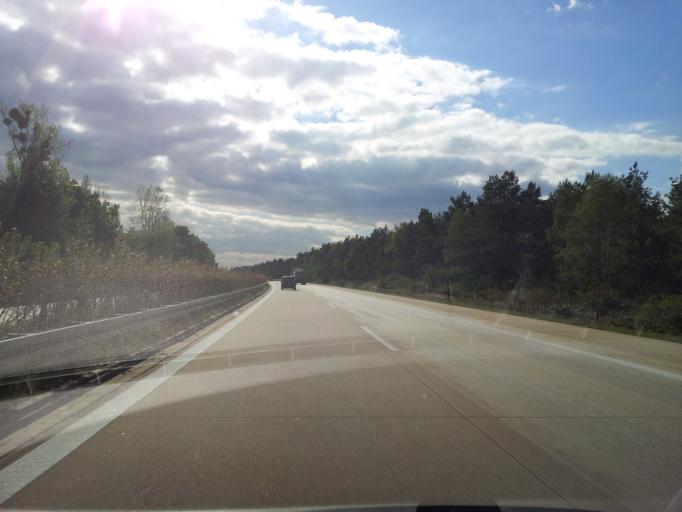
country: DE
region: Brandenburg
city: Schwarzheide
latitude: 51.4863
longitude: 13.8828
